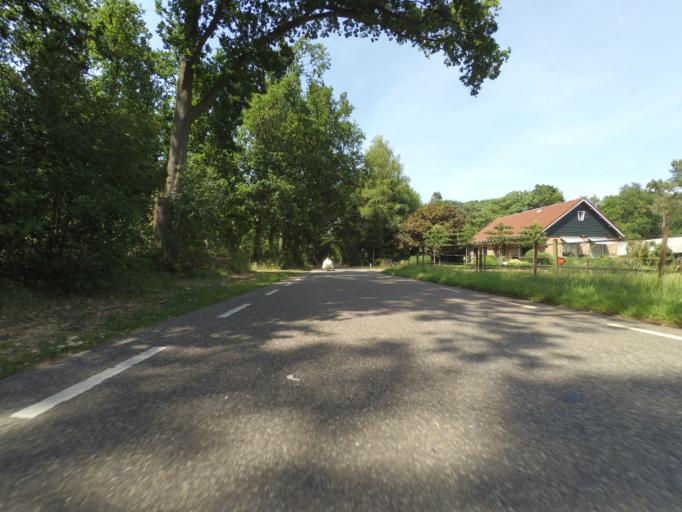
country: NL
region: North Brabant
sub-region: Gemeente Bergen op Zoom
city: Bergen op Zoom
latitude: 51.4837
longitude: 4.3293
